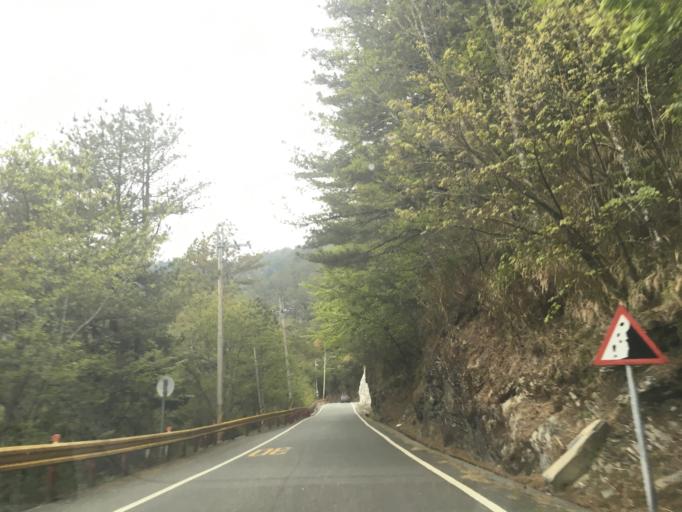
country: TW
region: Taiwan
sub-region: Hualien
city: Hualian
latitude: 24.1866
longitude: 121.3311
